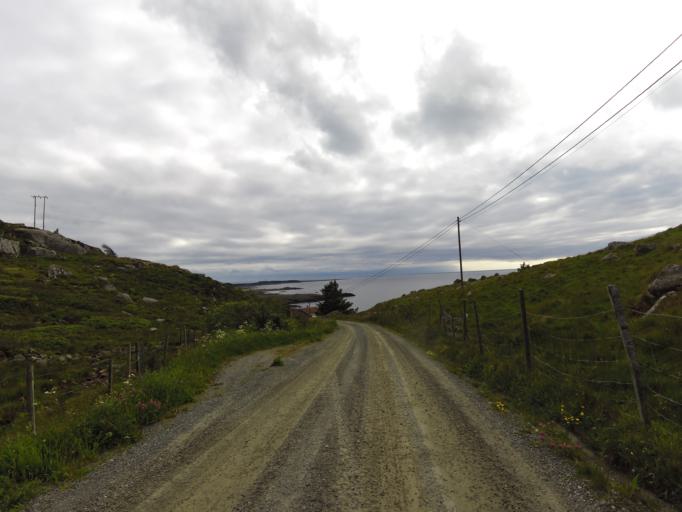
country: NO
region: Vest-Agder
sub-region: Farsund
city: Vestbygd
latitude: 58.1489
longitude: 6.6154
